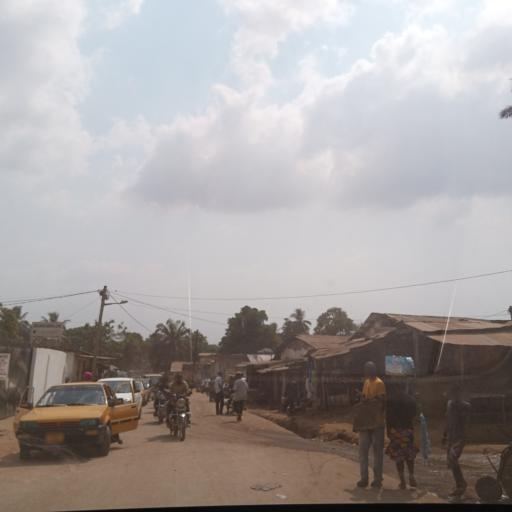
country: LR
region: Montserrado
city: Monrovia
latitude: 6.2902
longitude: -10.6899
